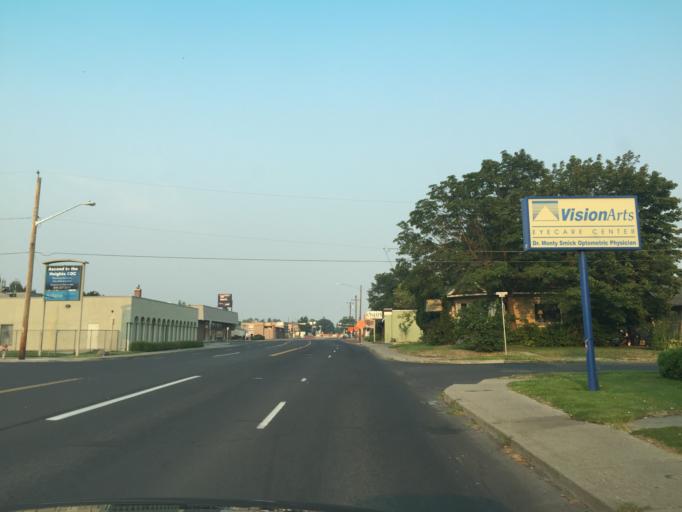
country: US
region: Washington
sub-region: Spokane County
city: Spokane
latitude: 47.6750
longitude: -117.4148
